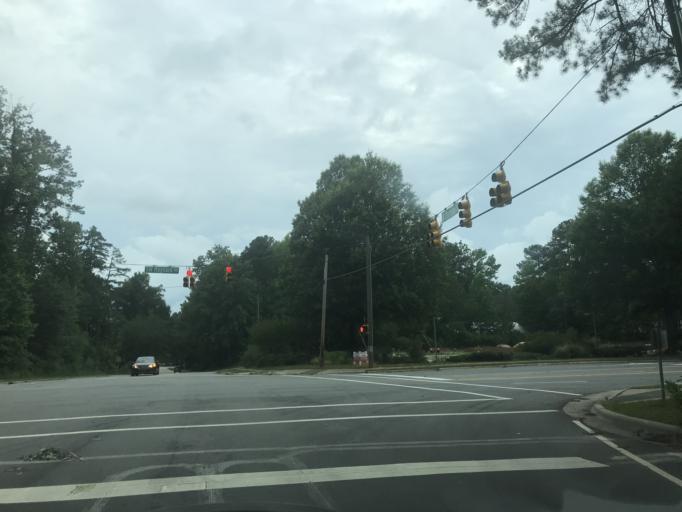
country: US
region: North Carolina
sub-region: Wake County
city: Cary
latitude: 35.7761
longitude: -78.8014
